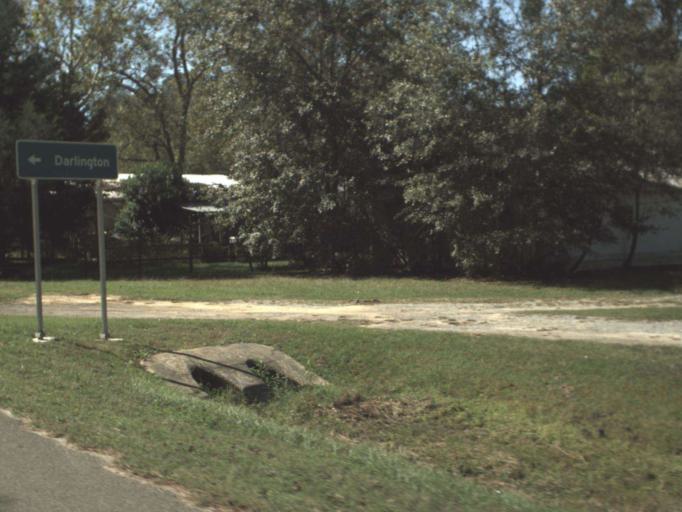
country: US
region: Alabama
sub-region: Geneva County
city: Samson
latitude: 30.9717
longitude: -86.1355
